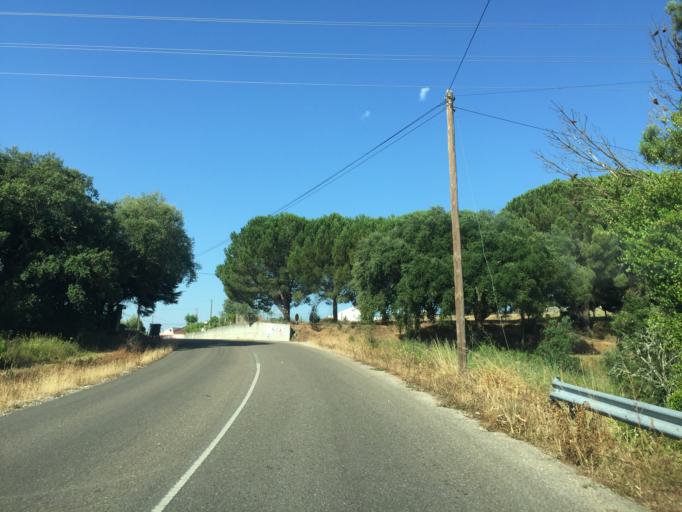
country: PT
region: Santarem
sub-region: Tomar
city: Tomar
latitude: 39.5920
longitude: -8.3478
